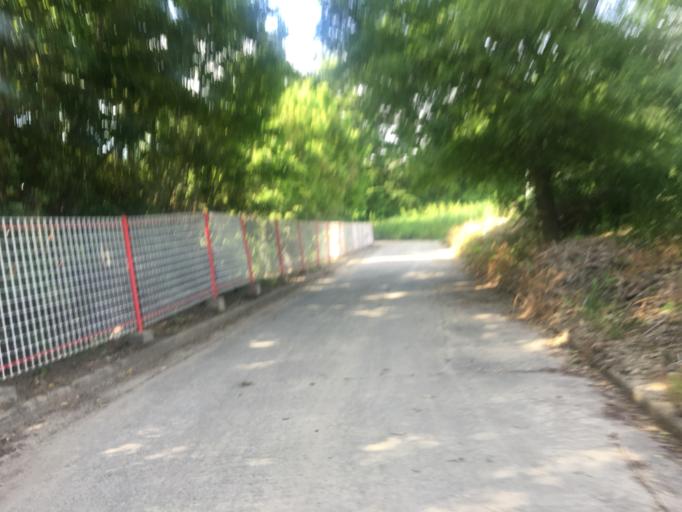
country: JP
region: Saitama
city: Shiki
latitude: 35.8537
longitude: 139.6004
